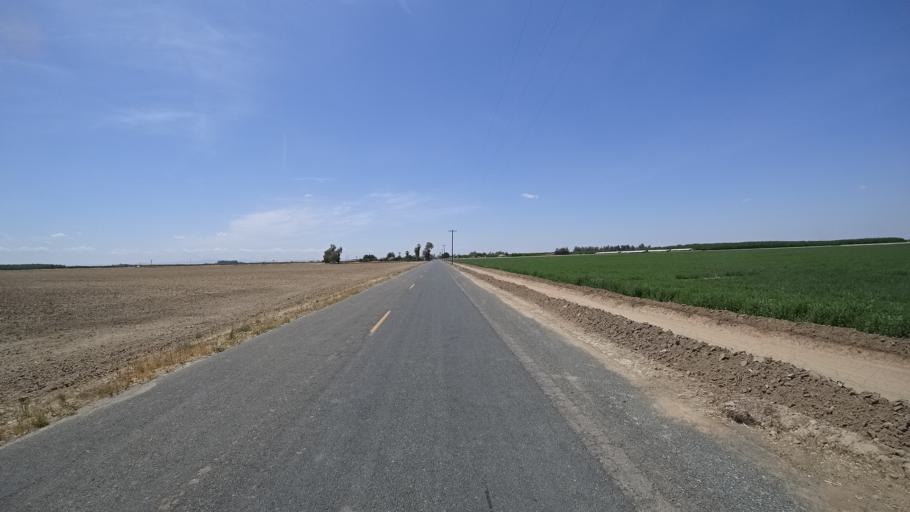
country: US
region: California
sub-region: Kings County
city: Home Garden
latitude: 36.2840
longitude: -119.6761
